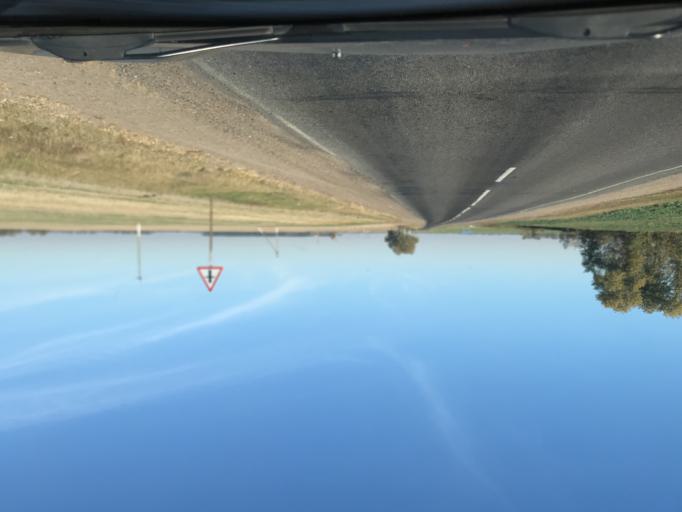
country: BY
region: Gomel
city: Brahin
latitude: 51.7984
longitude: 30.1381
